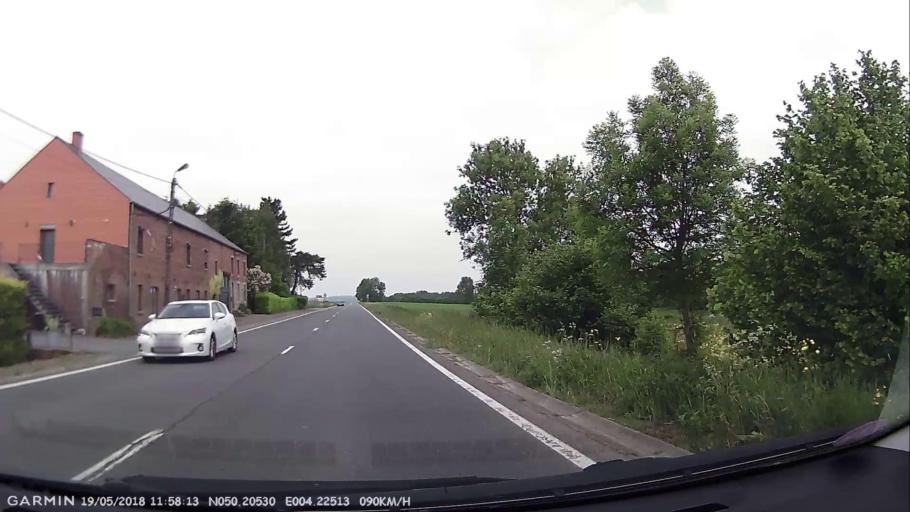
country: BE
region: Wallonia
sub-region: Province du Hainaut
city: Beaumont
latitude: 50.2056
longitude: 4.2252
